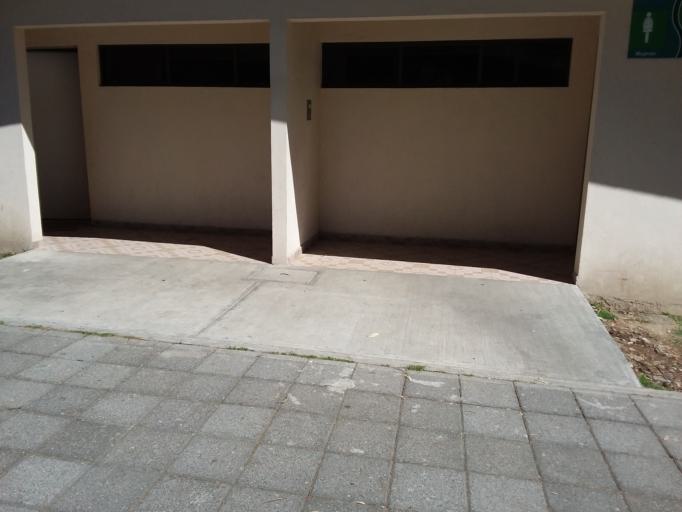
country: MX
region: Mexico
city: Toluca
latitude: 19.2719
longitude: -99.6549
